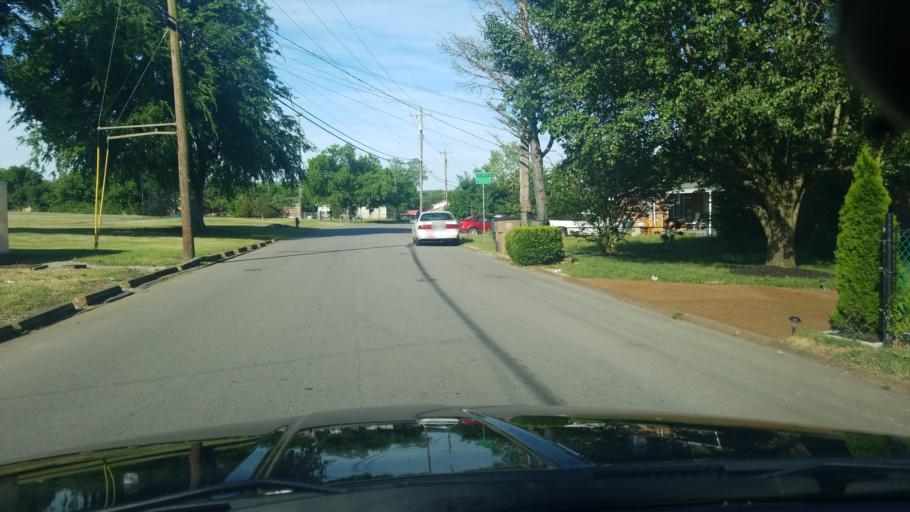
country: US
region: Tennessee
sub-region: Davidson County
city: Nashville
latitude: 36.2362
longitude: -86.7718
